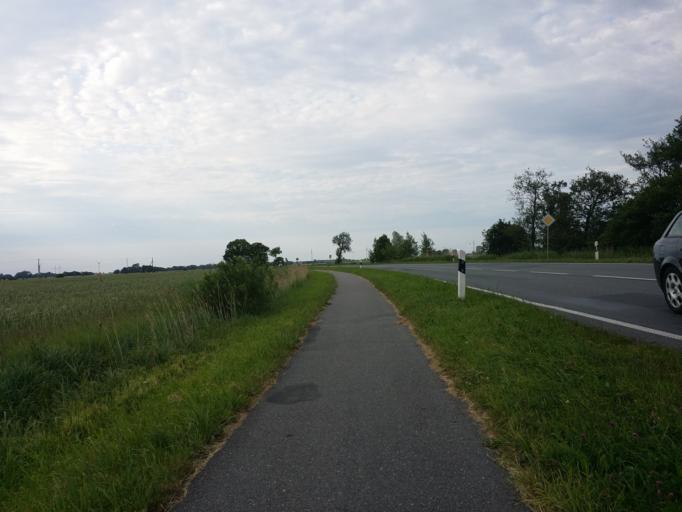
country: DE
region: Lower Saxony
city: Wittmund
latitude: 53.6053
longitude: 7.7960
